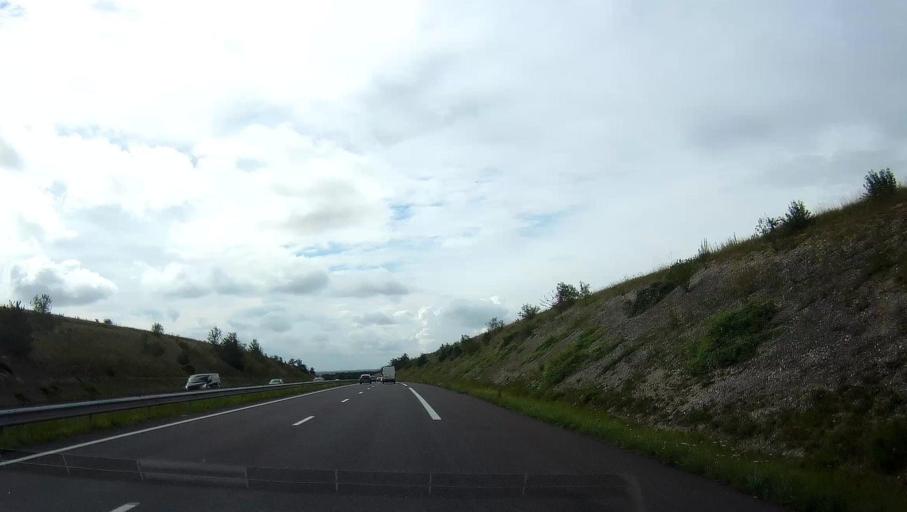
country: FR
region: Champagne-Ardenne
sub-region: Departement de la Marne
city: Fagnieres
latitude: 49.0406
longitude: 4.2810
